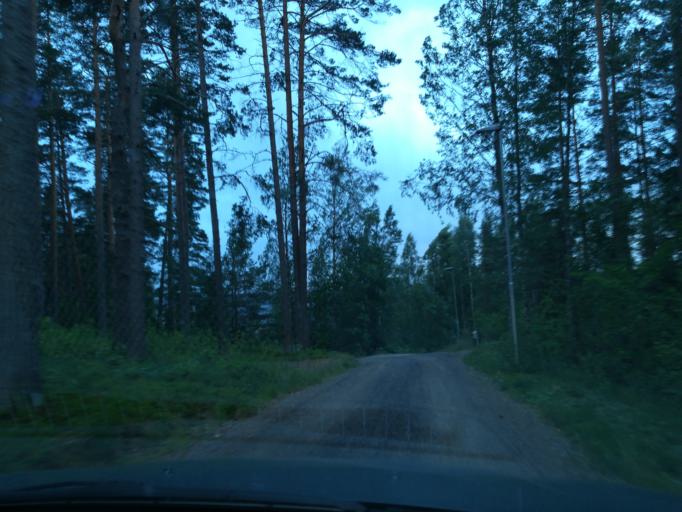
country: FI
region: Southern Savonia
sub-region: Mikkeli
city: Ristiina
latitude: 61.4978
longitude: 27.2704
